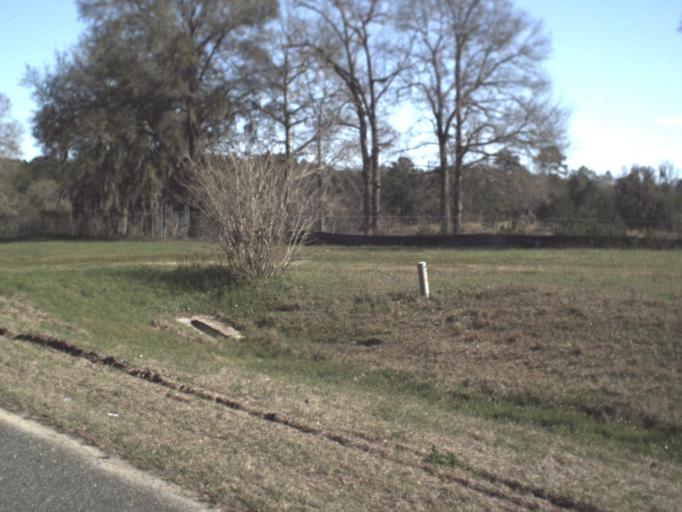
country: US
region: Florida
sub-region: Gadsden County
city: Midway
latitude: 30.5524
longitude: -84.5002
